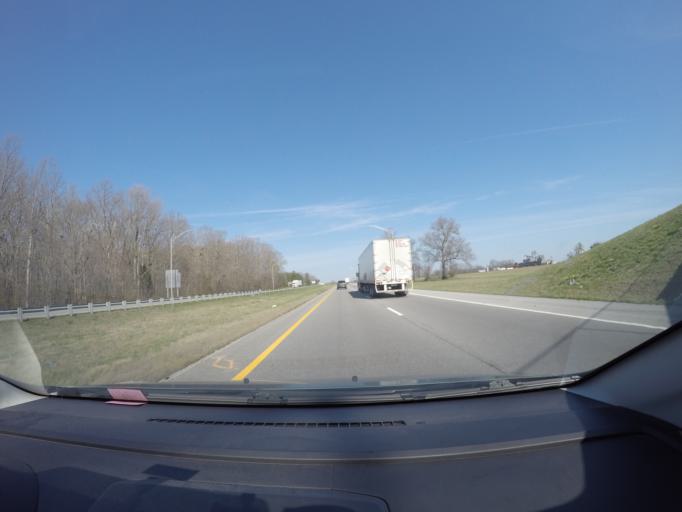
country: US
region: Tennessee
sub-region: Coffee County
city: Manchester
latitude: 35.4904
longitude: -86.0742
